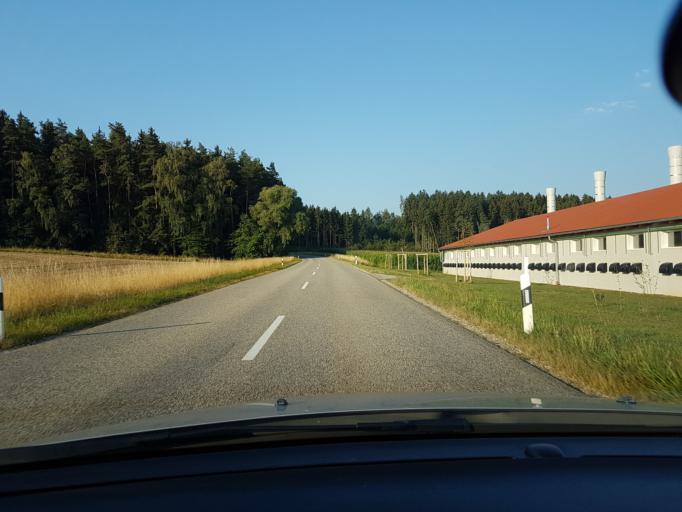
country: DE
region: Bavaria
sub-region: Lower Bavaria
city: Aham
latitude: 48.4888
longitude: 12.4644
